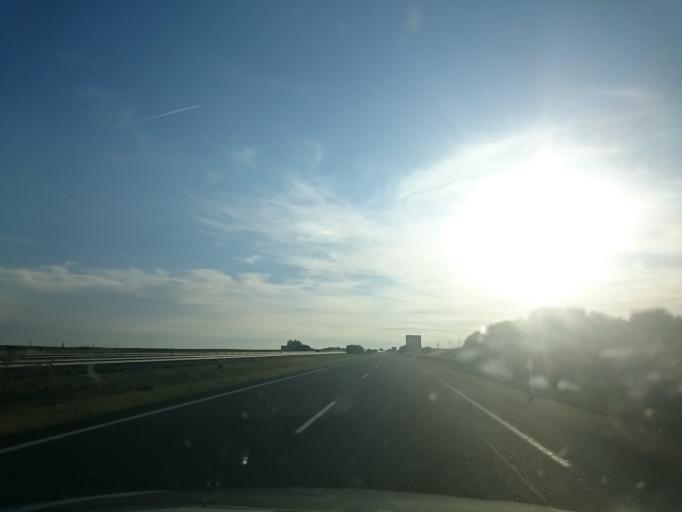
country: ES
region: Castille and Leon
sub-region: Provincia de Palencia
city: Moratinos
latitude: 42.3666
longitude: -4.9616
